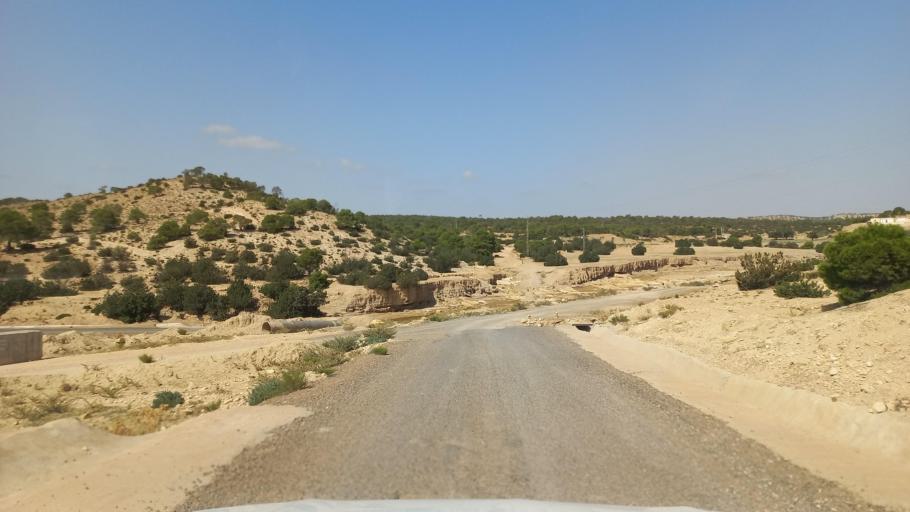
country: TN
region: Al Qasrayn
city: Sbiba
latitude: 35.3971
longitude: 8.9497
